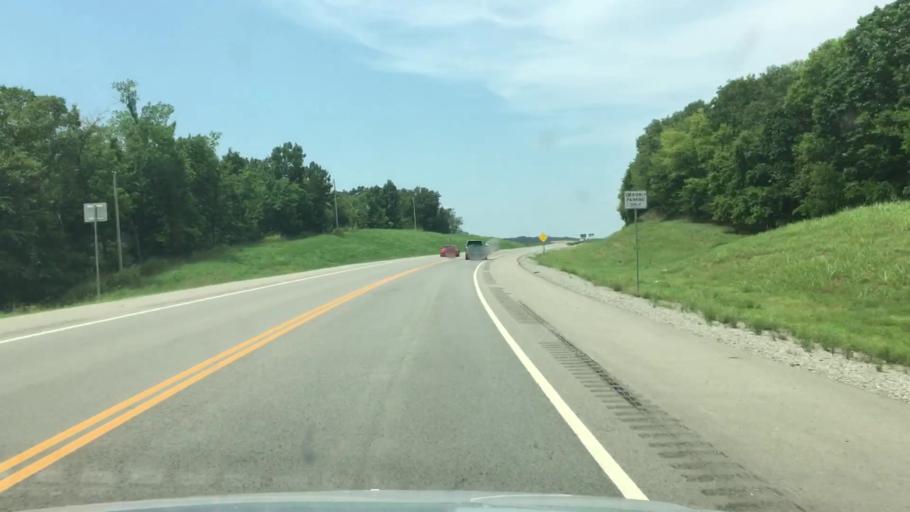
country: US
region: Oklahoma
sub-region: Wagoner County
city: Wagoner
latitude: 35.9284
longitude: -95.2622
